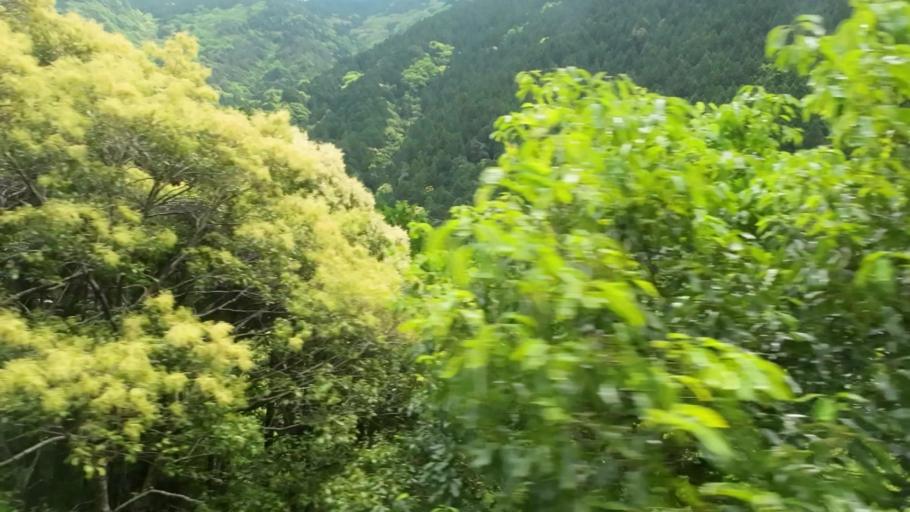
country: JP
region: Tokushima
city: Ikedacho
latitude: 33.9116
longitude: 133.7573
